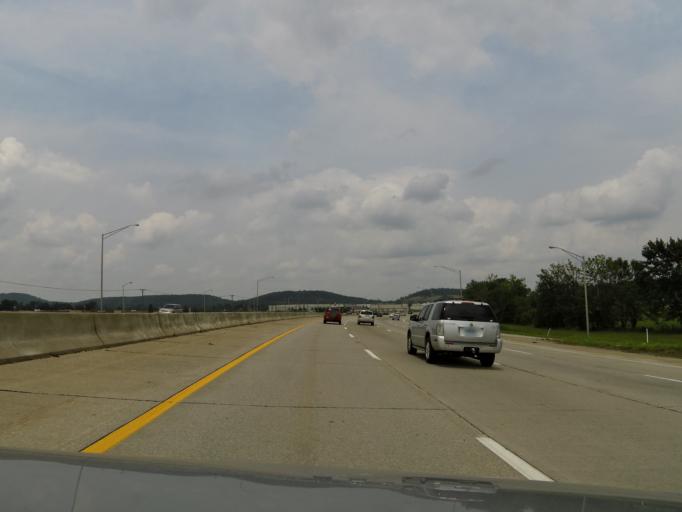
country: US
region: Kentucky
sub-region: Bullitt County
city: Shepherdsville
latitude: 37.9952
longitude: -85.7051
